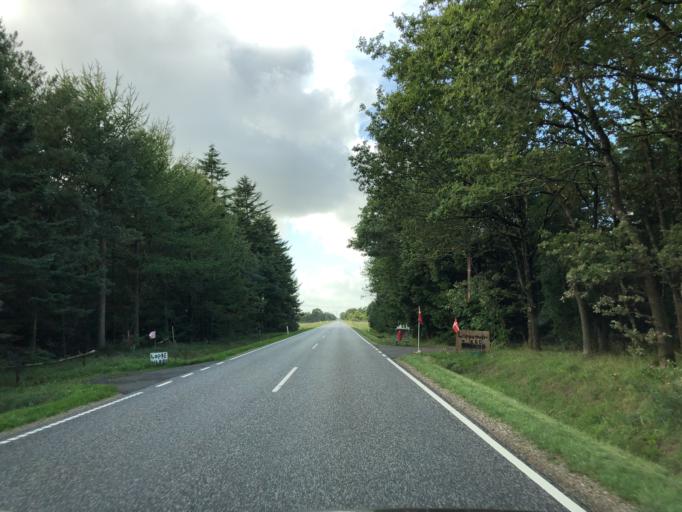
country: DK
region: Central Jutland
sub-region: Holstebro Kommune
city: Holstebro
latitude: 56.3699
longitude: 8.5576
